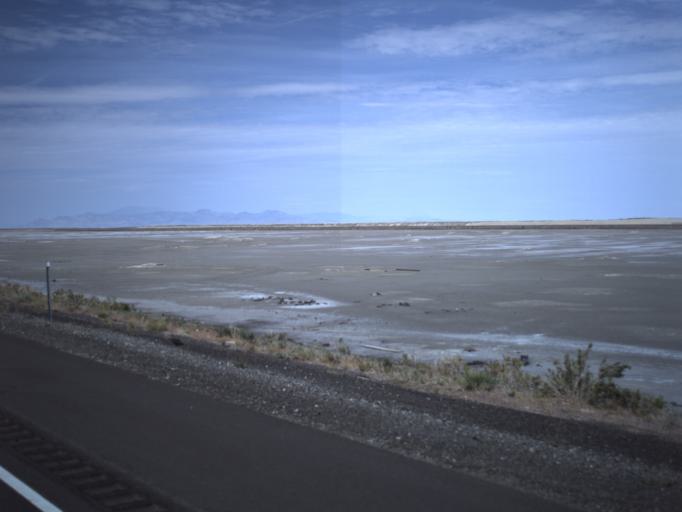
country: US
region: Utah
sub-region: Tooele County
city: Wendover
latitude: 40.7279
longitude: -113.2921
